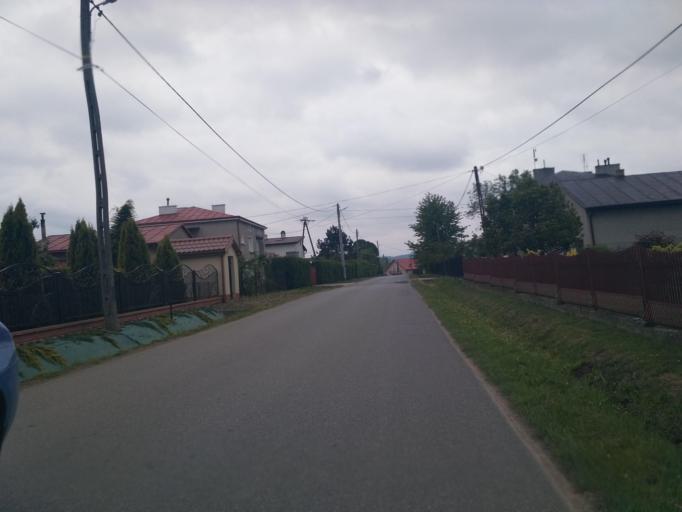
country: PL
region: Subcarpathian Voivodeship
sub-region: Powiat krosnienski
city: Chorkowka
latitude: 49.6669
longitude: 21.7201
